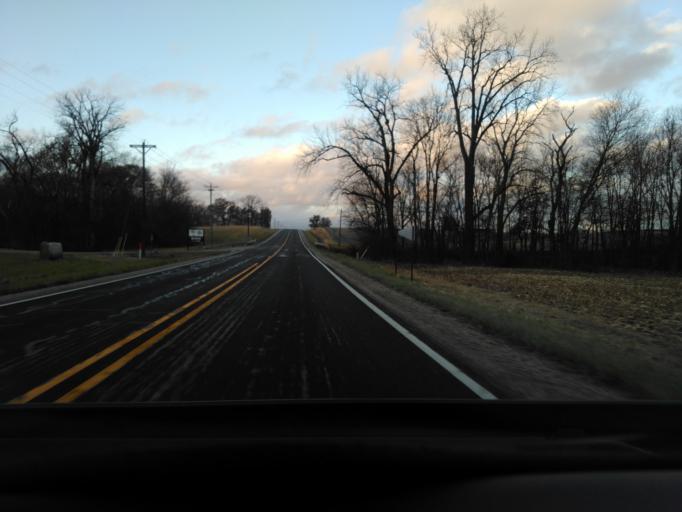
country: US
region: Illinois
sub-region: Effingham County
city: Altamont
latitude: 38.9821
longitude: -88.7489
